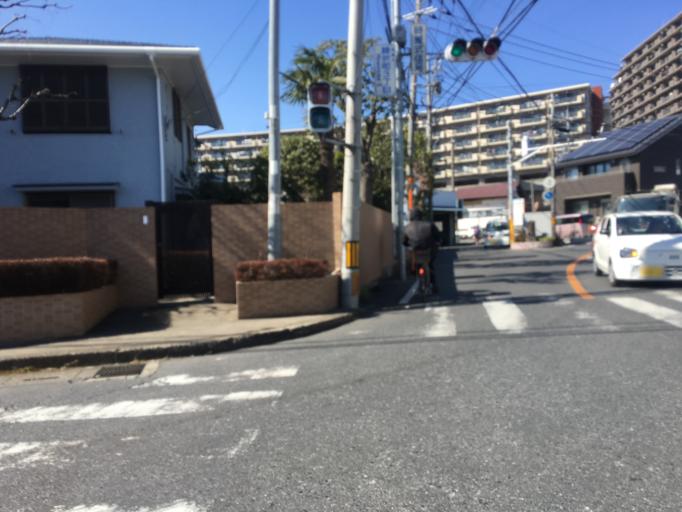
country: JP
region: Saitama
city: Asaka
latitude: 35.7957
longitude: 139.5780
